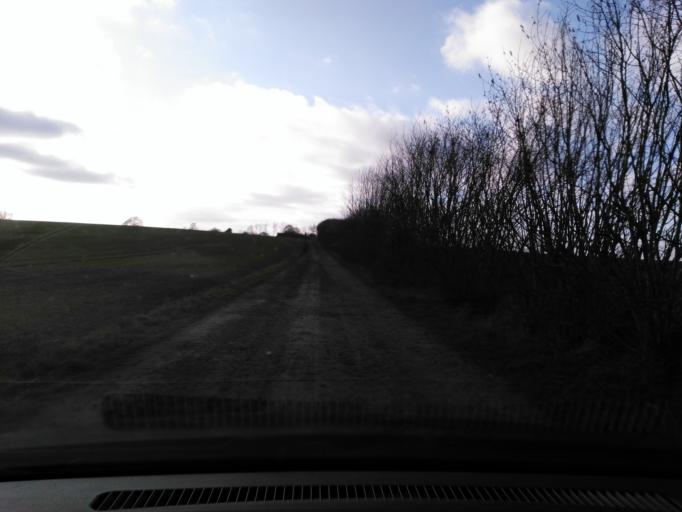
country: DE
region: Schleswig-Holstein
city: Klein Barkau
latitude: 54.2729
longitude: 10.1231
